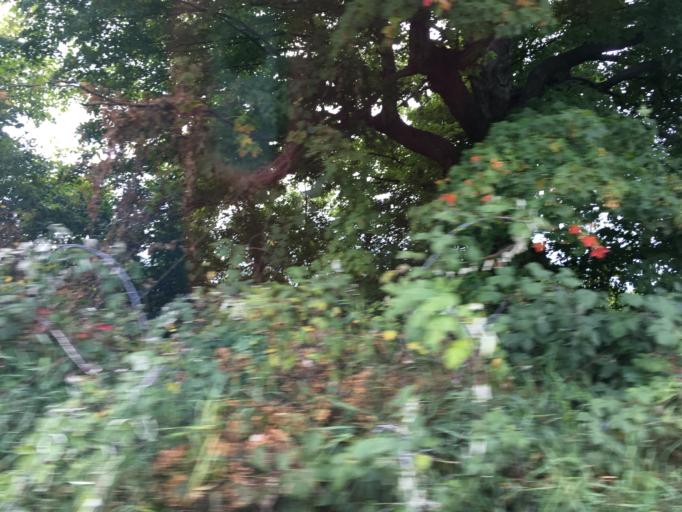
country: US
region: Michigan
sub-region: Lapeer County
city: Barnes Lake-Millers Lake
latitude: 43.3296
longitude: -83.3497
